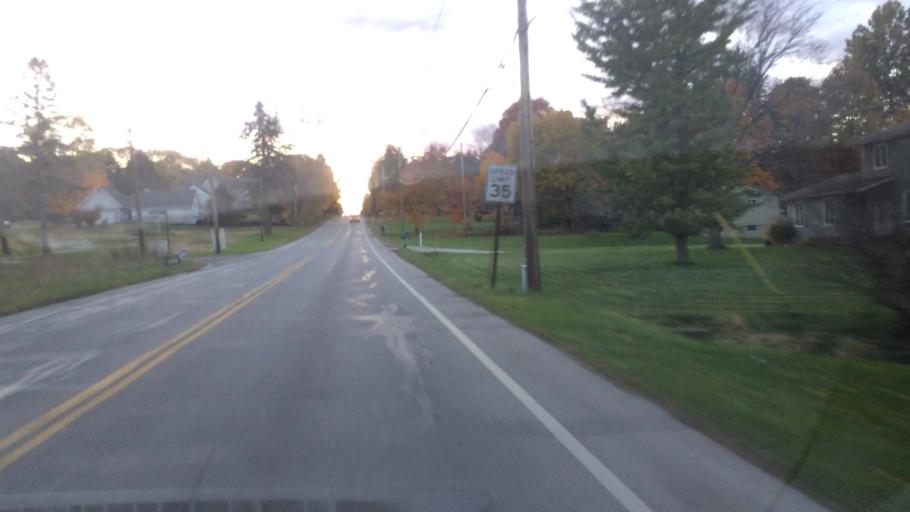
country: US
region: Ohio
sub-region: Summit County
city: Norton
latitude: 41.0500
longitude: -81.6501
